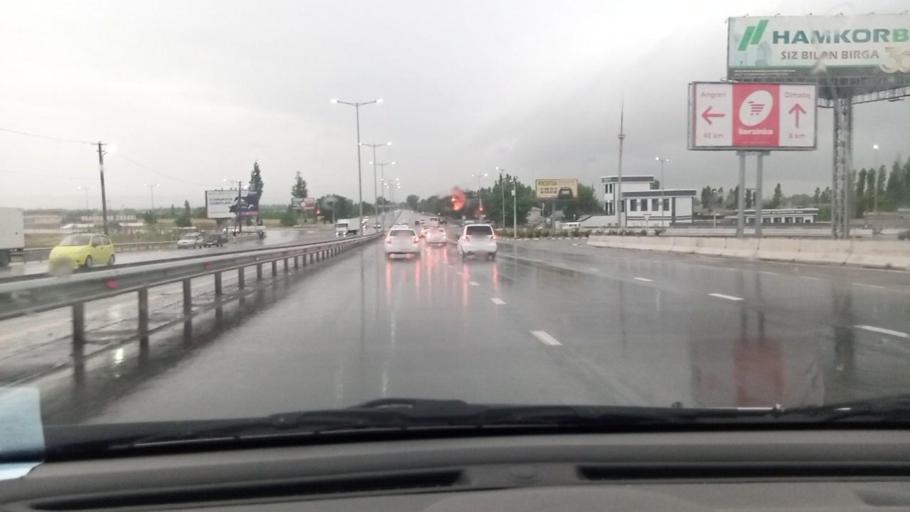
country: UZ
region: Toshkent
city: Ohangaron
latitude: 40.9218
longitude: 69.5970
